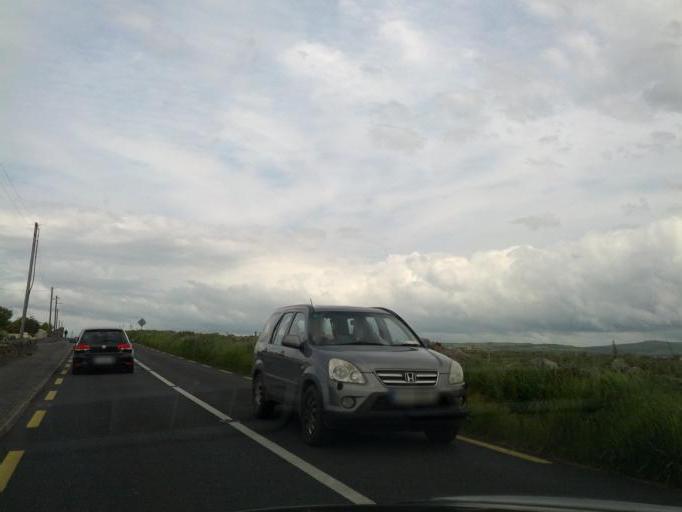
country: IE
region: Munster
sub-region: An Clar
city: Kilrush
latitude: 52.8471
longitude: -9.4171
